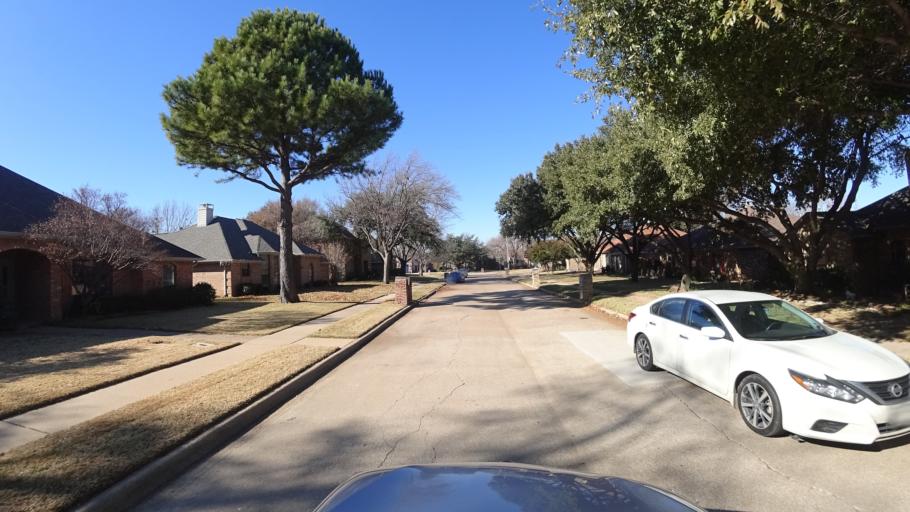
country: US
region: Texas
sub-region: Denton County
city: Lewisville
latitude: 33.0183
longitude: -97.0254
